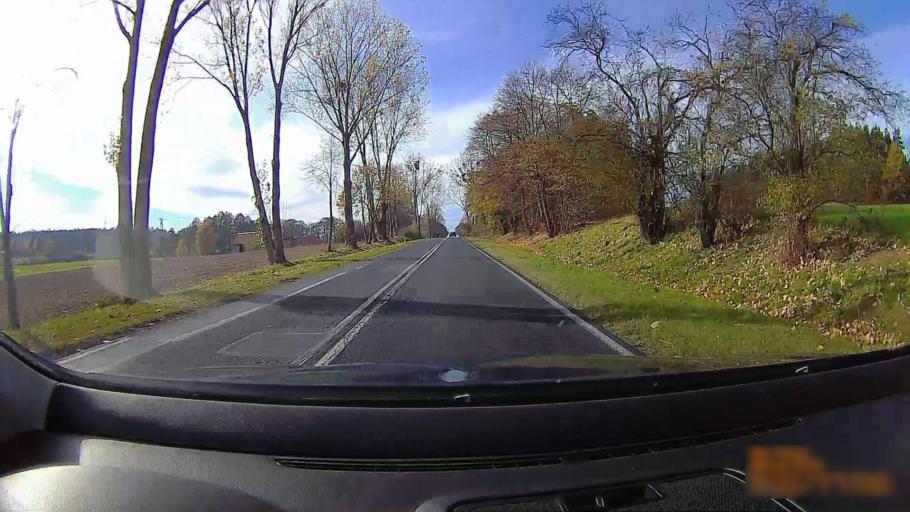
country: PL
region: Greater Poland Voivodeship
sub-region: Powiat ostrzeszowski
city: Ostrzeszow
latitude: 51.4331
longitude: 17.9658
